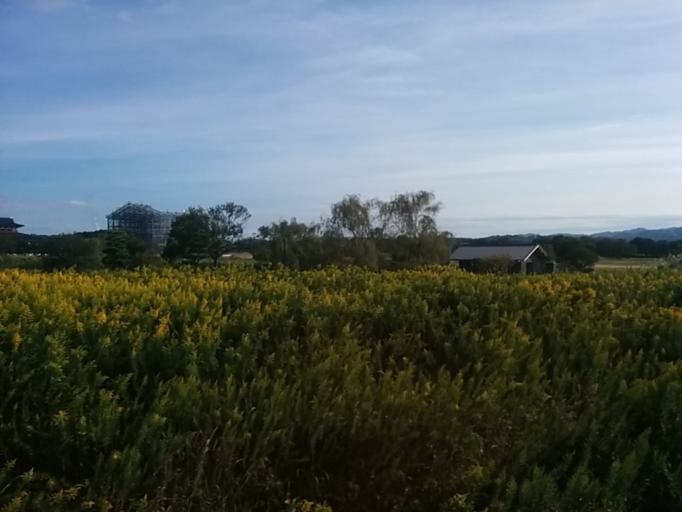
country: JP
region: Nara
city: Nara-shi
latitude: 34.6891
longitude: 135.7919
